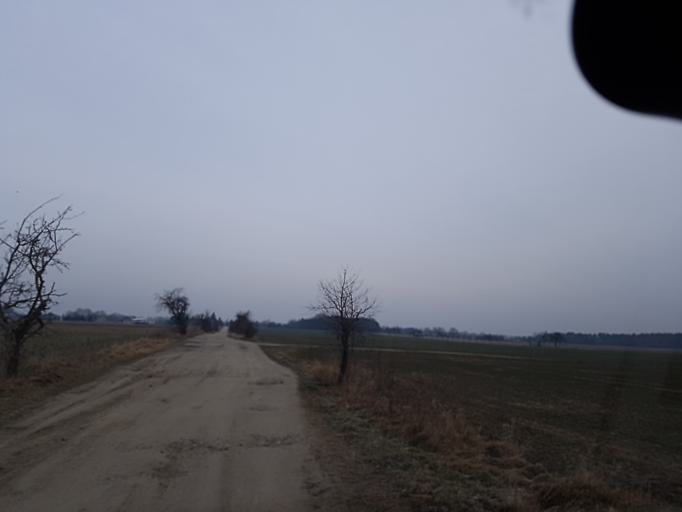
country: DE
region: Brandenburg
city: Ruckersdorf
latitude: 51.5840
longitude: 13.5432
